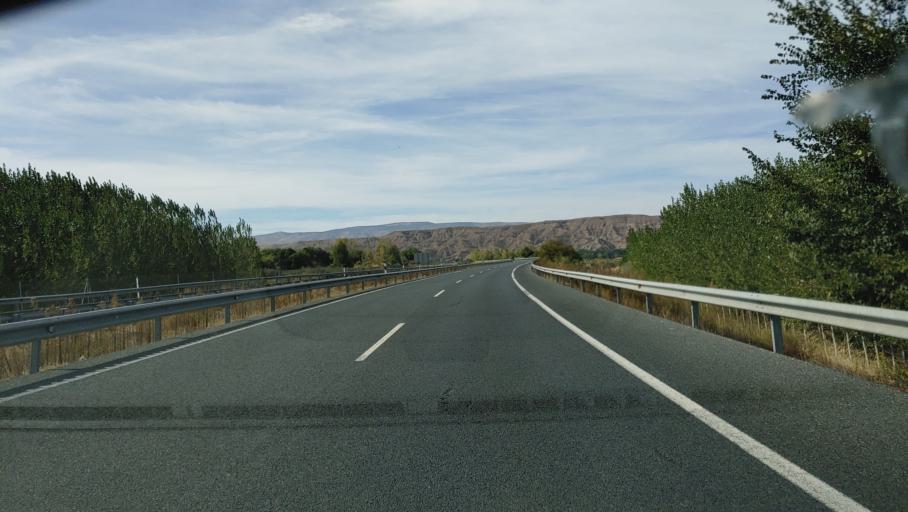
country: ES
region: Andalusia
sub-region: Provincia de Granada
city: Purullena
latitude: 37.3258
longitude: -3.1738
